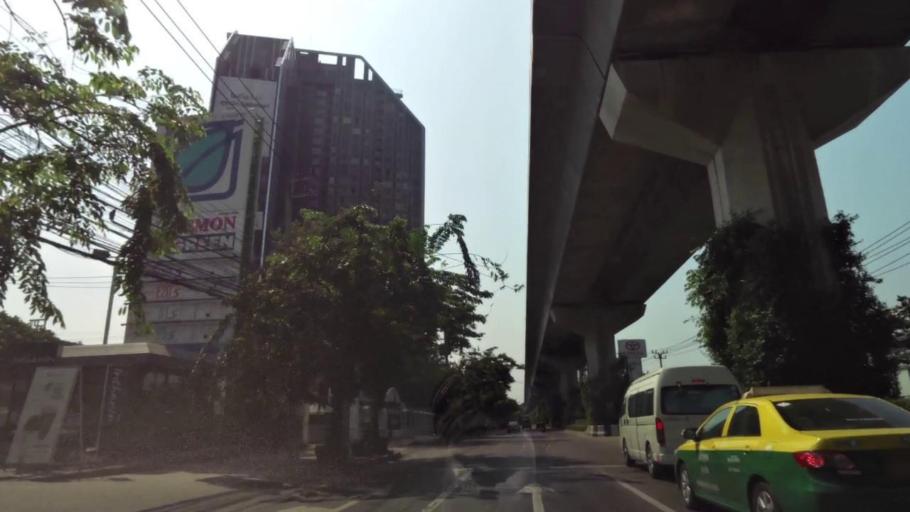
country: TH
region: Bangkok
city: Phra Khanong
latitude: 13.6665
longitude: 100.6041
